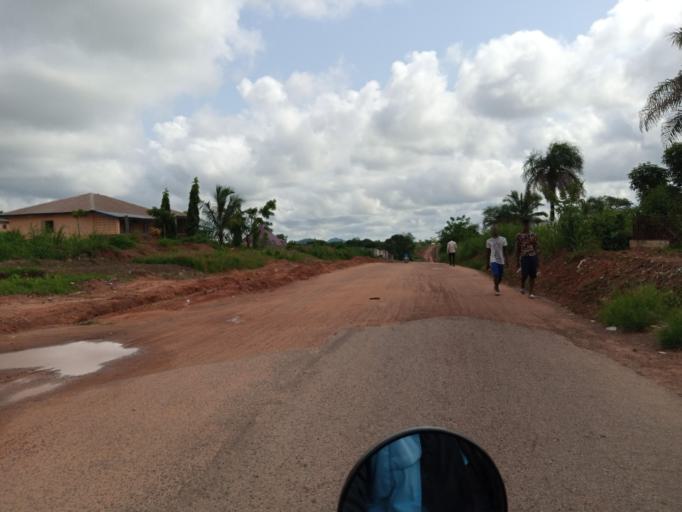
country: SL
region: Southern Province
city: Bo
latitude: 7.9847
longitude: -11.7375
